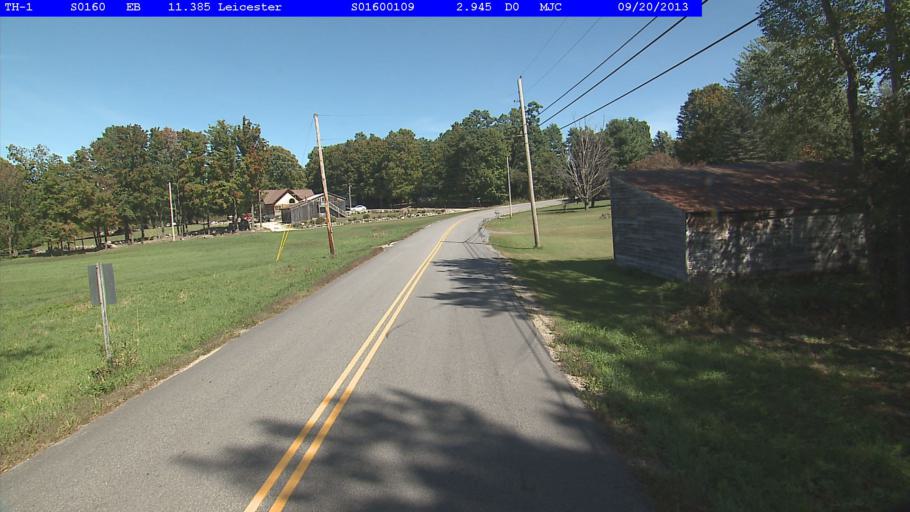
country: US
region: Vermont
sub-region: Rutland County
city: Brandon
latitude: 43.8650
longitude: -73.1111
